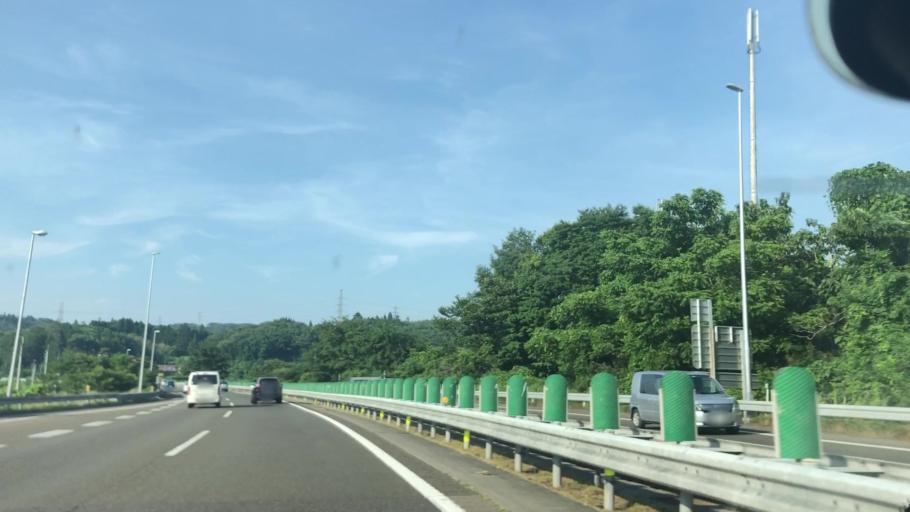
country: JP
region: Miyagi
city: Iwanuma
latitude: 38.1698
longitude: 140.7683
